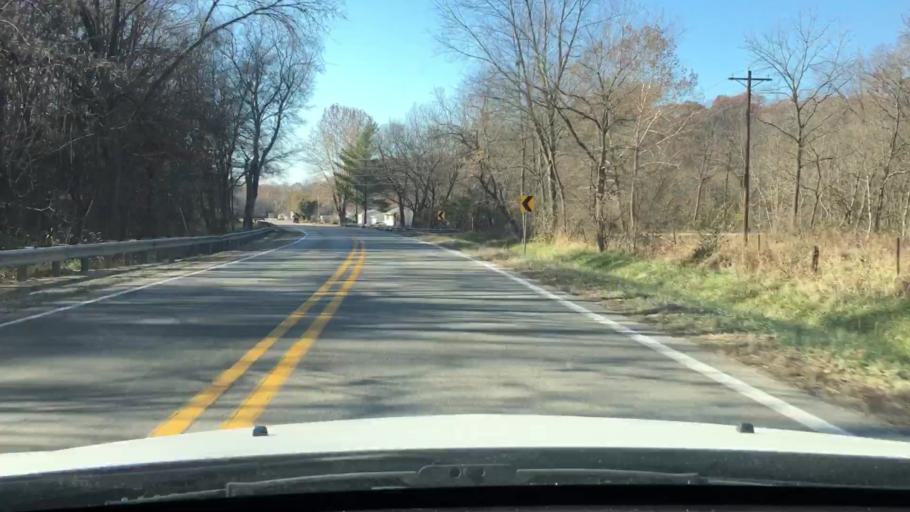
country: US
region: Missouri
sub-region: Pike County
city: Louisiana
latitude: 39.5186
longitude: -90.9537
